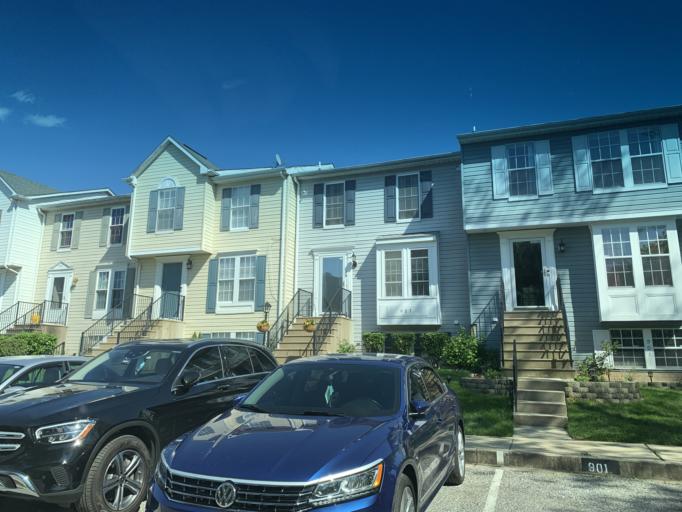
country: US
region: Maryland
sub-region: Harford County
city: Edgewood
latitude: 39.4380
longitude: -76.2889
